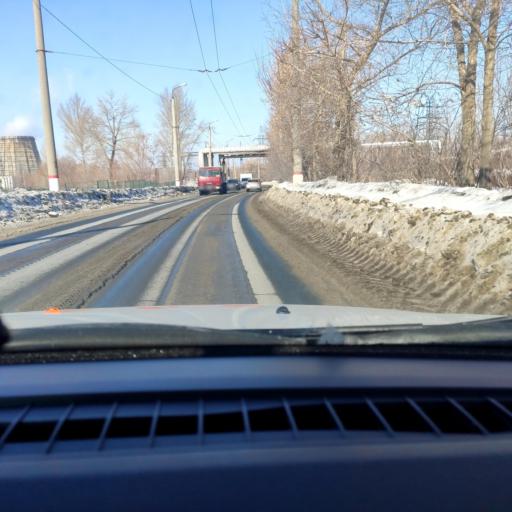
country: RU
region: Samara
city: Novokuybyshevsk
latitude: 53.1074
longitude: 49.9295
